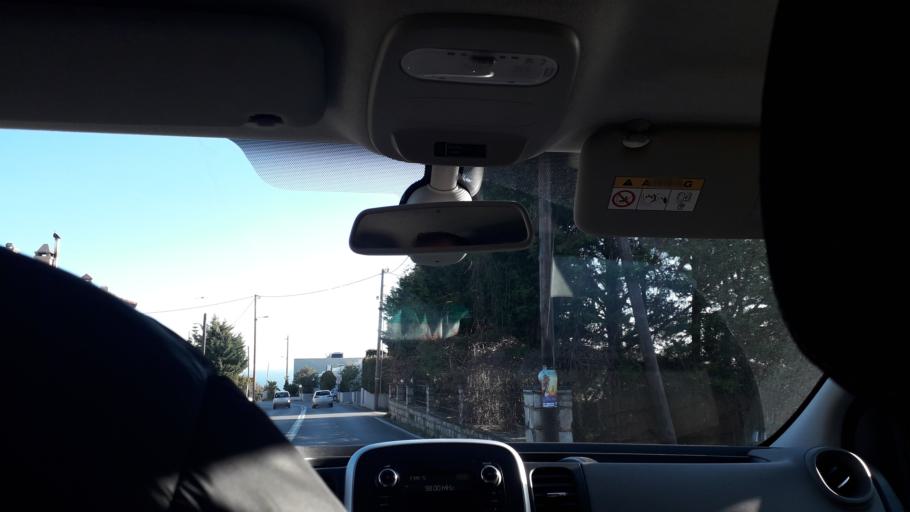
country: GR
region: Crete
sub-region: Nomos Rethymnis
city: Atsipopoulon
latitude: 35.3573
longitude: 24.4402
